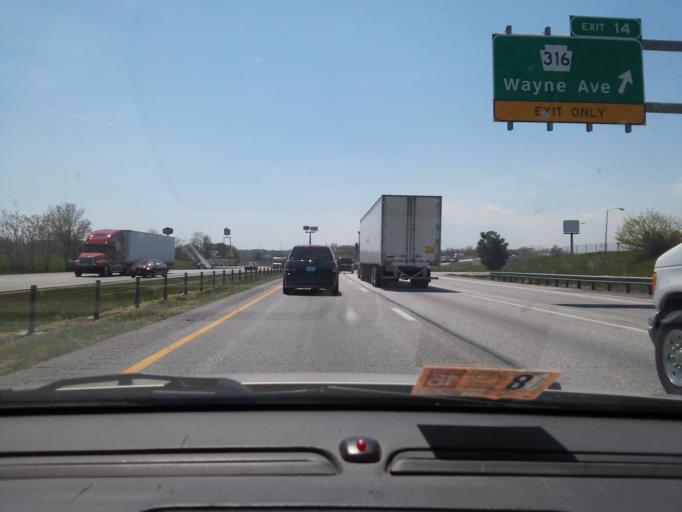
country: US
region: Pennsylvania
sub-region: Franklin County
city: Chambersburg
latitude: 39.9124
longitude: -77.6451
